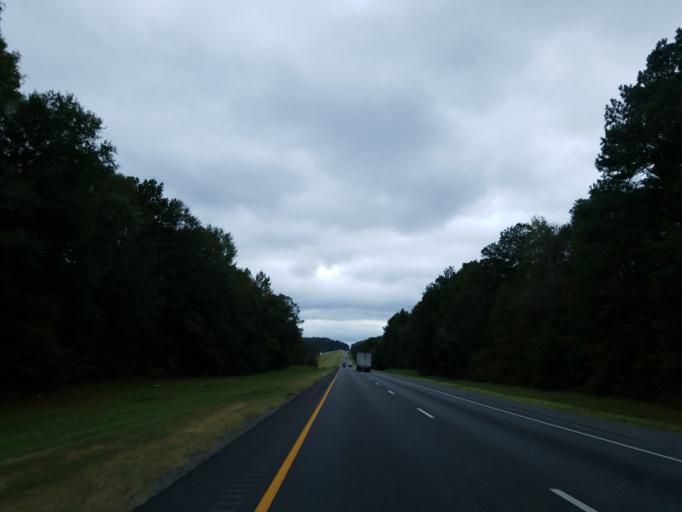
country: US
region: Alabama
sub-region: Hale County
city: Moundville
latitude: 33.0017
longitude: -87.7692
